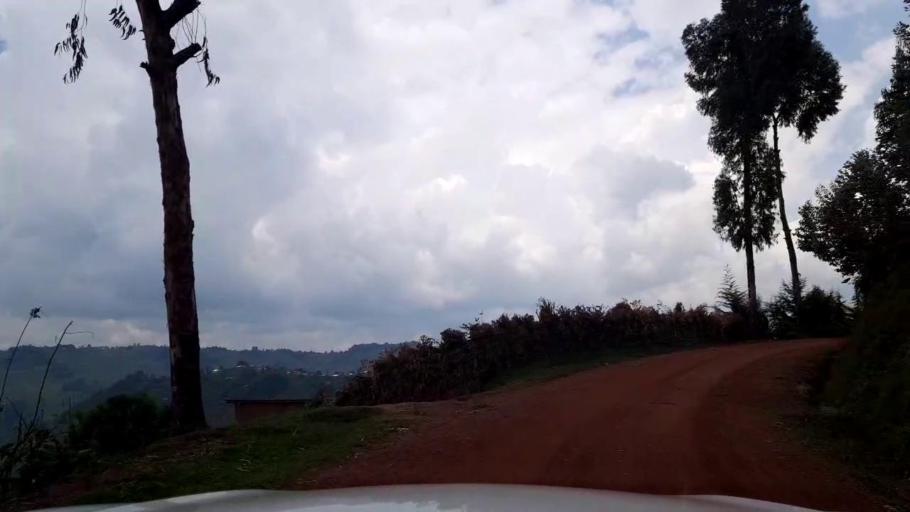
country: RW
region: Northern Province
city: Byumba
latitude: -1.5218
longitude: 29.9508
